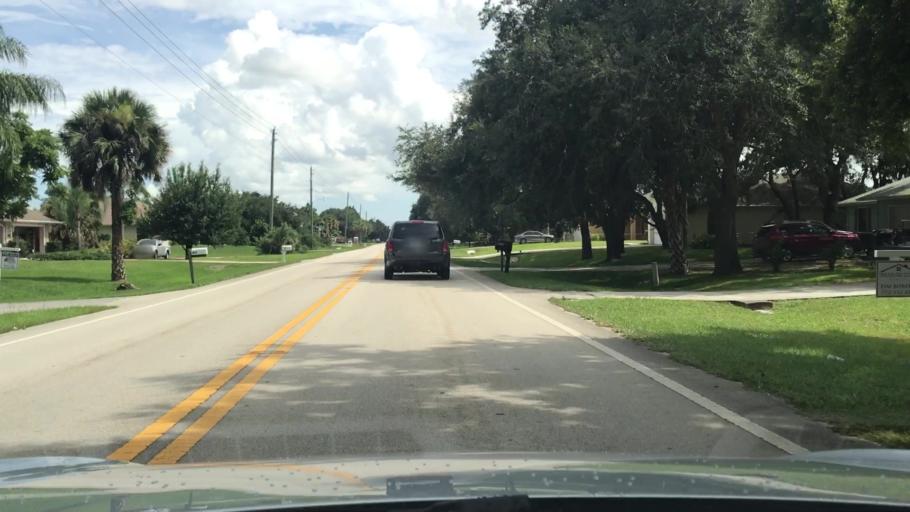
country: US
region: Florida
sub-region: Indian River County
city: Sebastian
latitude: 27.7886
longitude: -80.4989
